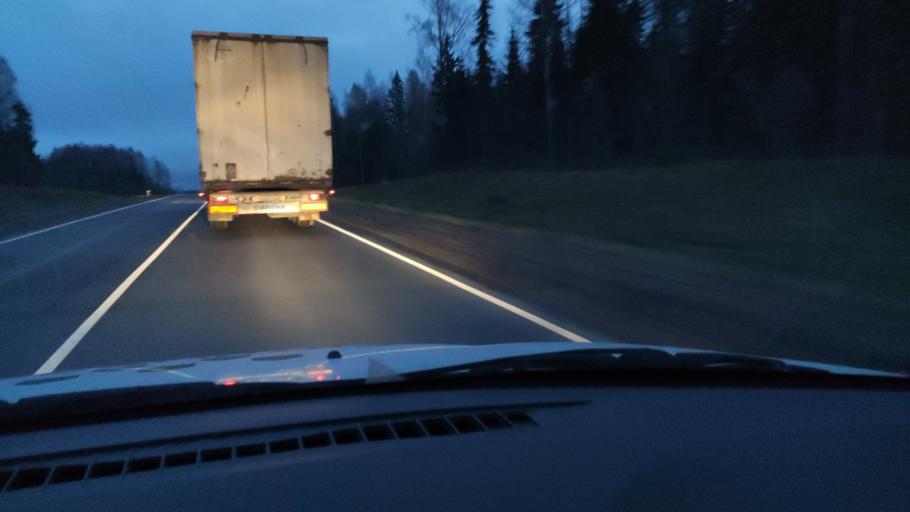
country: RU
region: Kirov
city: Kostino
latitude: 58.8331
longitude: 53.5044
